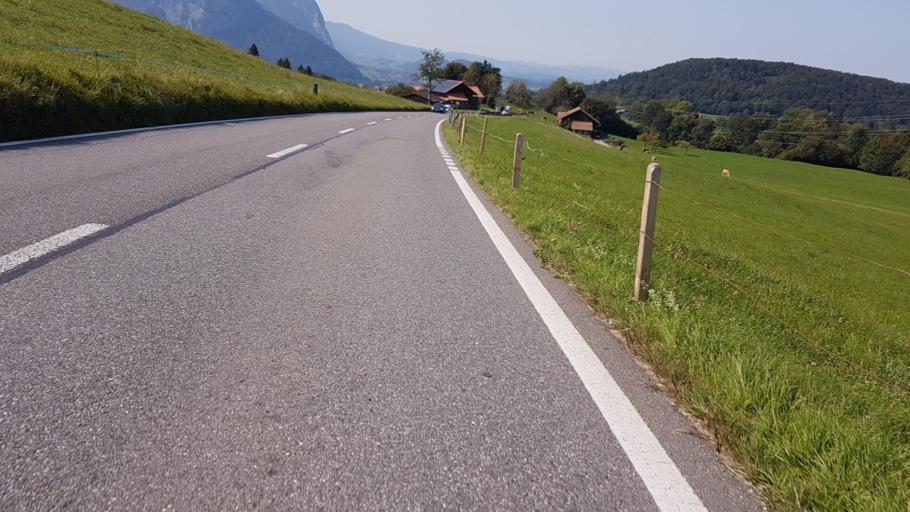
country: CH
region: Bern
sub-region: Frutigen-Niedersimmental District
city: Aeschi
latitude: 46.6636
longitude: 7.6887
